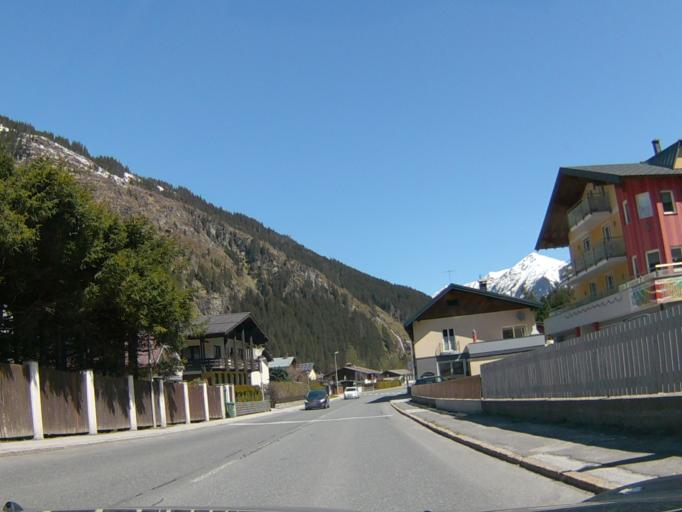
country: AT
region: Salzburg
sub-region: Politischer Bezirk Sankt Johann im Pongau
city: Bad Gastein
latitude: 47.0910
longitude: 13.1207
